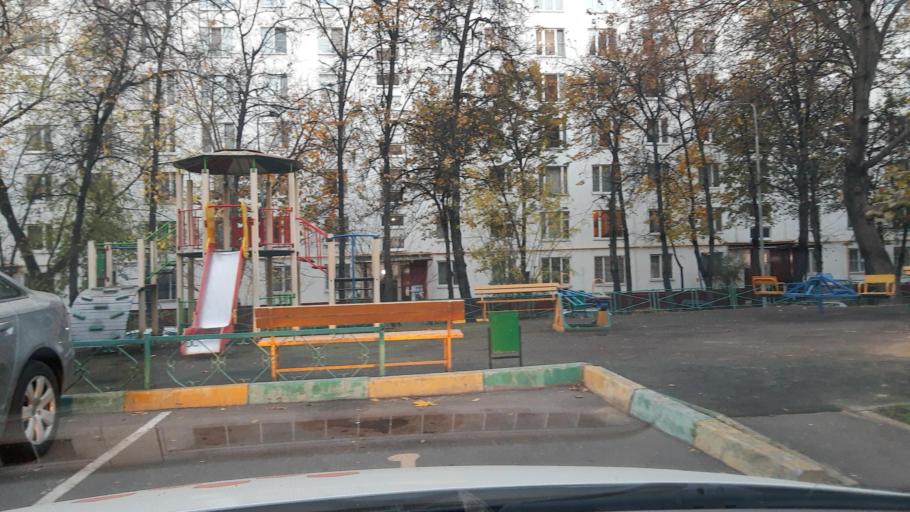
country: RU
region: Moscow
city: Tekstil'shchiki
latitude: 55.6974
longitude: 37.7355
